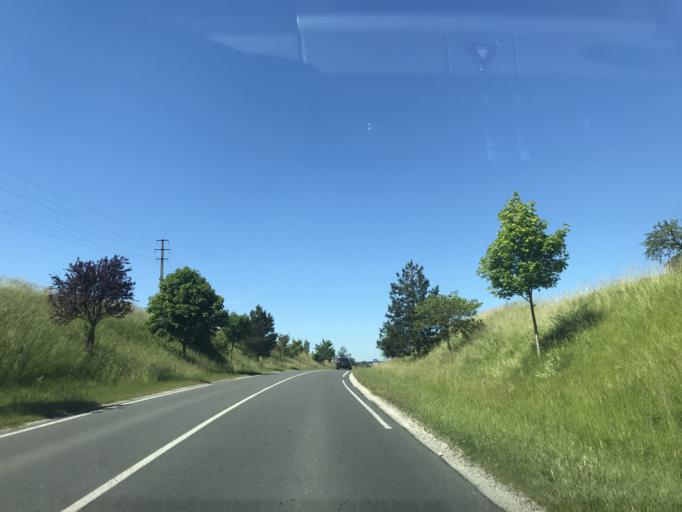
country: FR
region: Poitou-Charentes
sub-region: Departement de la Charente-Maritime
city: Pons
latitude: 45.5737
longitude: -0.5356
